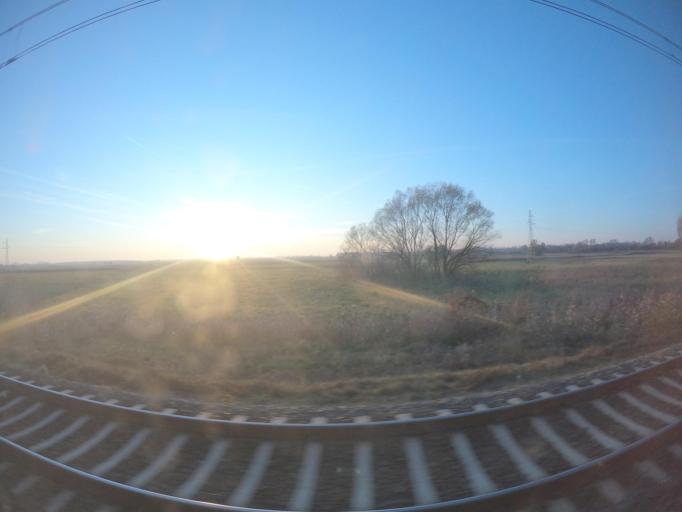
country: PL
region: Lubusz
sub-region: Powiat gorzowski
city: Kostrzyn nad Odra
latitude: 52.5608
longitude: 14.6484
